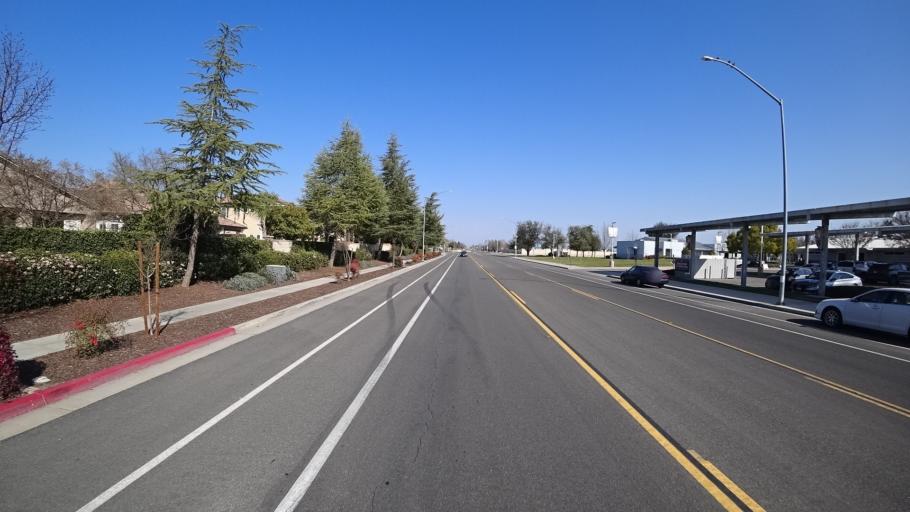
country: US
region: California
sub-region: Fresno County
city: Clovis
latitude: 36.8799
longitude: -119.7389
